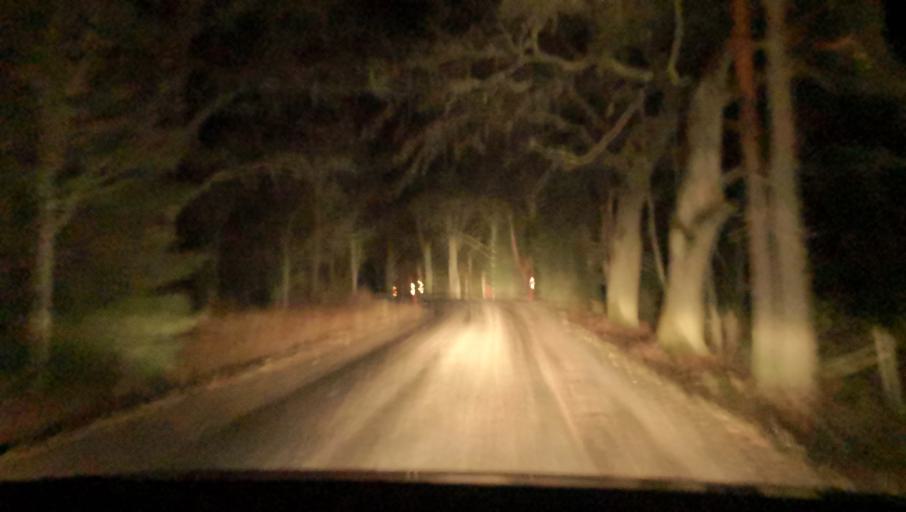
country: SE
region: Vaestmanland
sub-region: Vasteras
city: Tillberga
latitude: 59.6698
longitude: 16.6392
